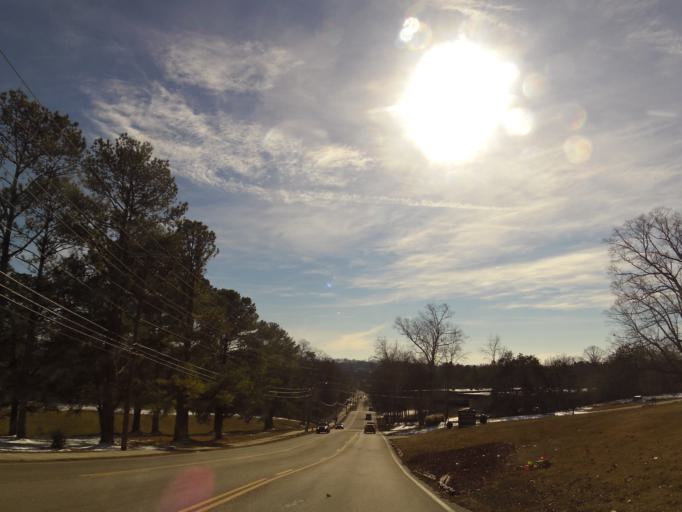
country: US
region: Tennessee
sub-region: Blount County
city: Louisville
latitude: 35.9204
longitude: -84.0591
